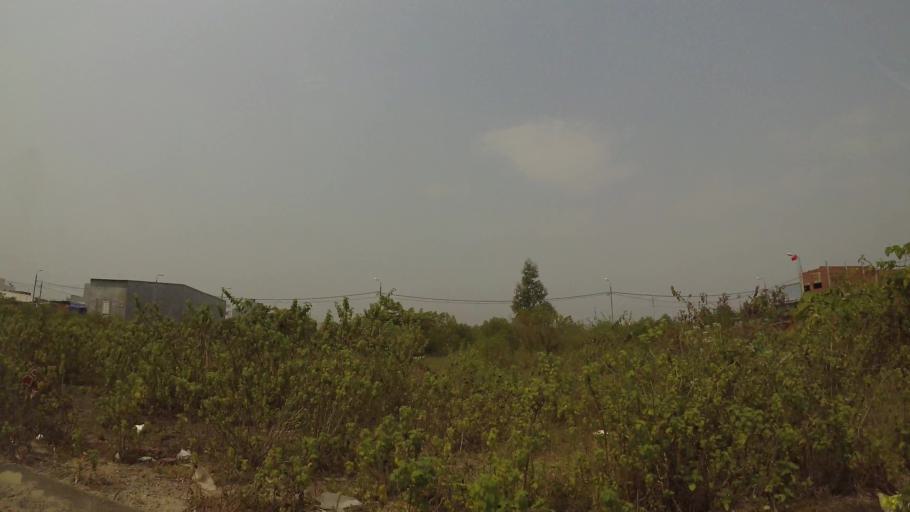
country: VN
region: Da Nang
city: Cam Le
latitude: 15.9812
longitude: 108.2202
